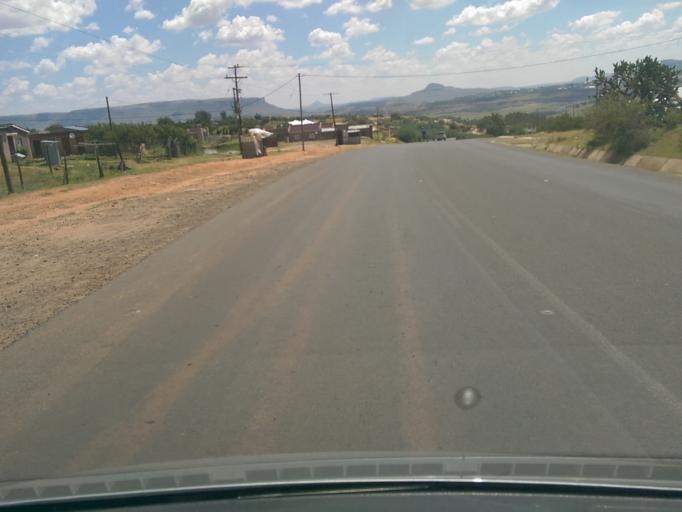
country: LS
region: Maseru
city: Maseru
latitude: -29.4090
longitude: 27.5814
